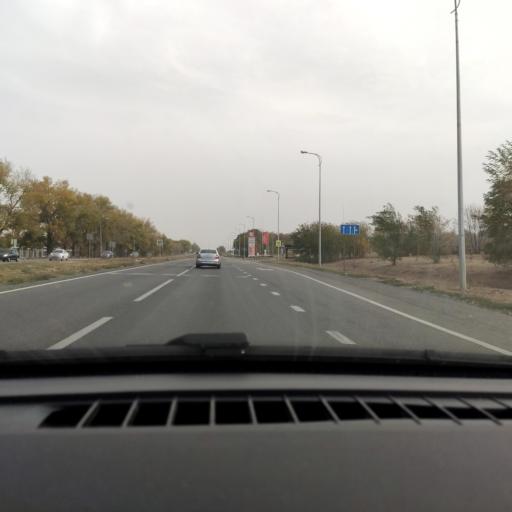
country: RU
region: Belgorod
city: Razumnoye
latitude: 50.6591
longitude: 36.6982
